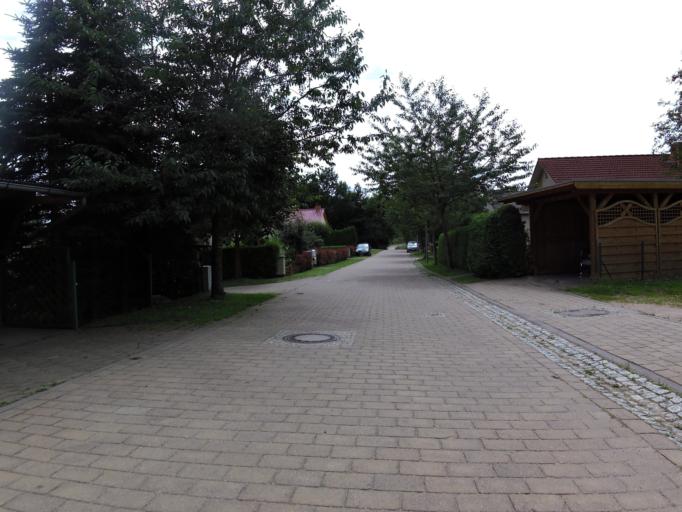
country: DE
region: Mecklenburg-Vorpommern
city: Loitz
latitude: 53.3420
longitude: 13.4285
